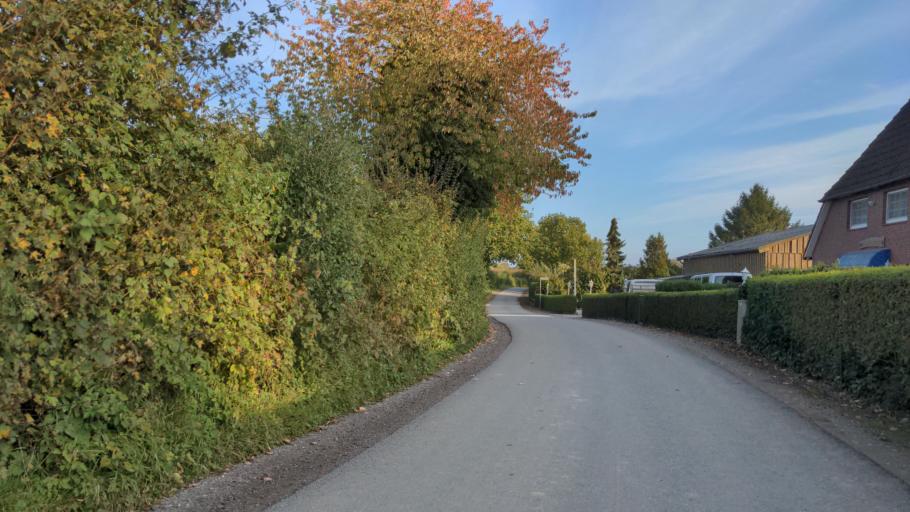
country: DE
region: Schleswig-Holstein
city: Manhagen
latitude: 54.1860
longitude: 10.9451
